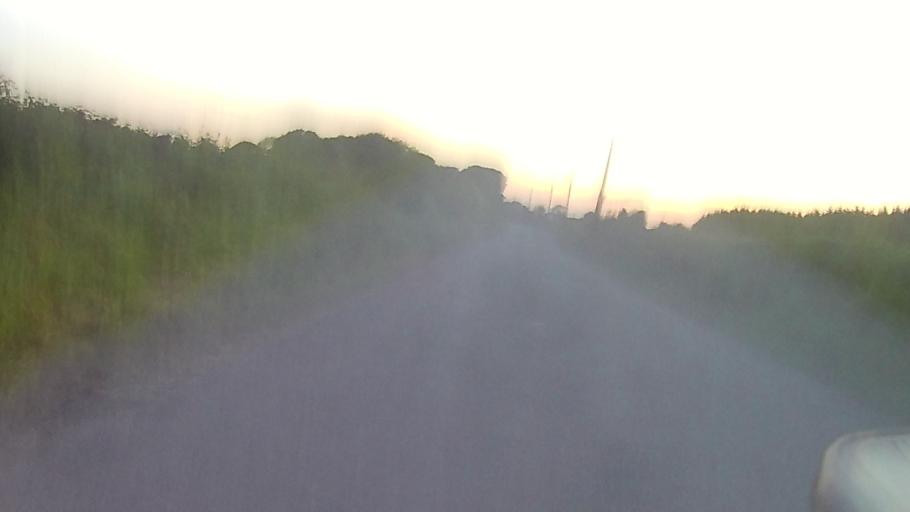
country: IE
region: Munster
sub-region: County Cork
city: Carrigtwohill
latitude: 51.9712
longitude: -8.2423
